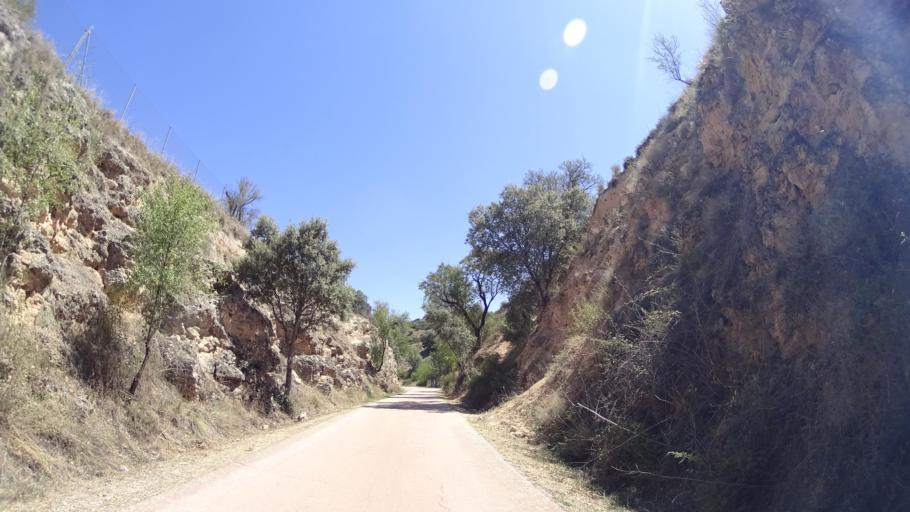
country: ES
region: Madrid
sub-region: Provincia de Madrid
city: Ambite
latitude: 40.2941
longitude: -3.1964
